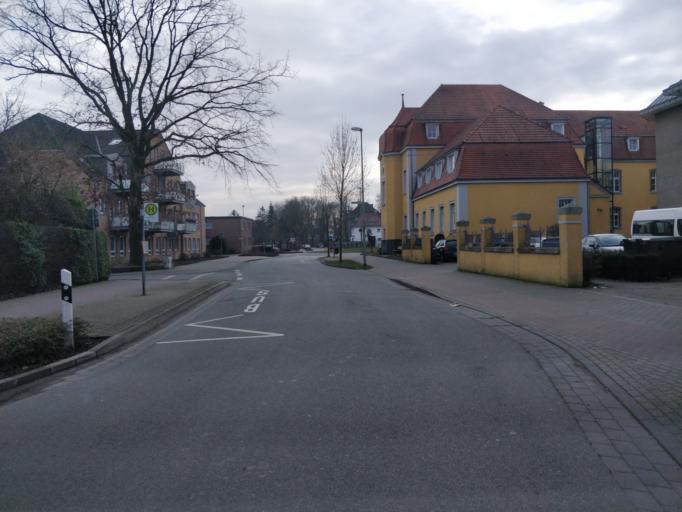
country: DE
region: North Rhine-Westphalia
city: Rees
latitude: 51.7636
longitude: 6.3994
